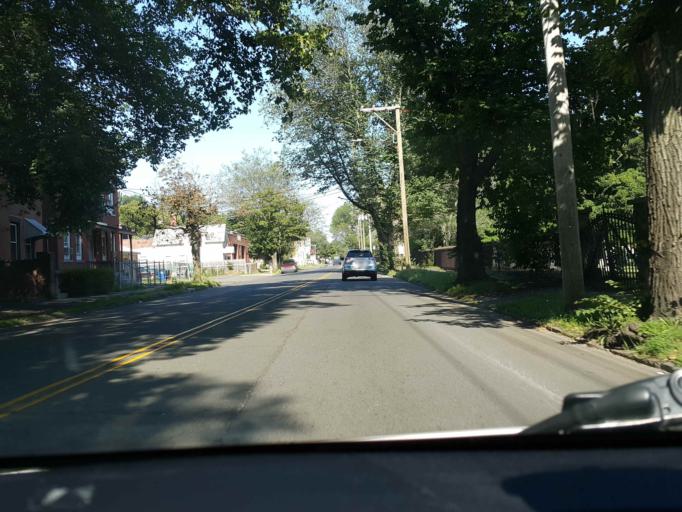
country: US
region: Connecticut
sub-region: New Haven County
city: New Haven
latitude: 41.2975
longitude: -72.9469
